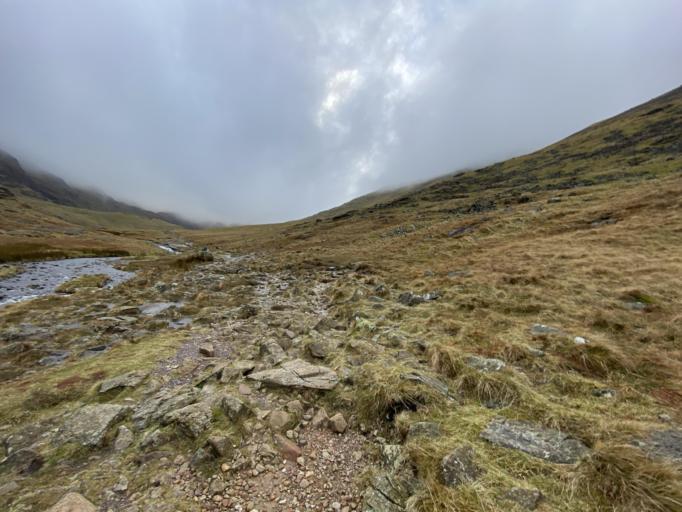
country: GB
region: England
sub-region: Cumbria
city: Keswick
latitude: 54.4814
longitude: -3.2013
